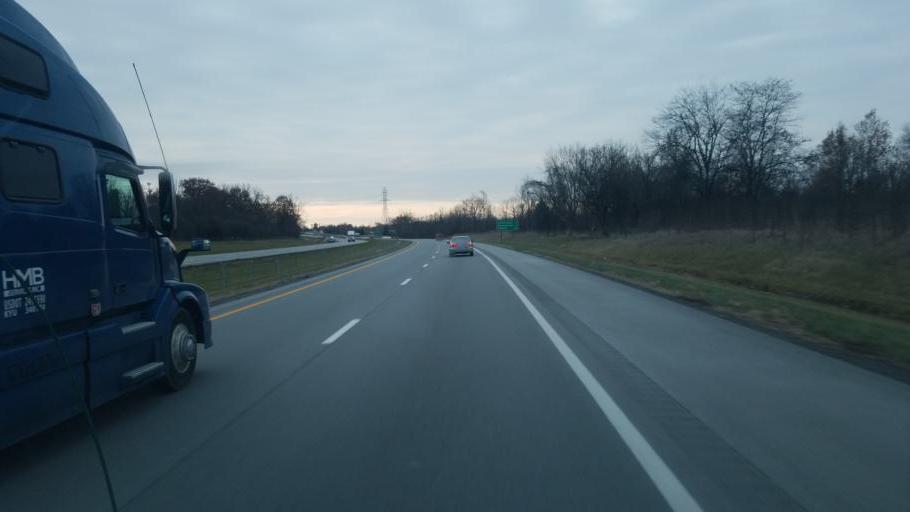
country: US
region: Ohio
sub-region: Allen County
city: Fort Shawnee
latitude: 40.6765
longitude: -84.1307
